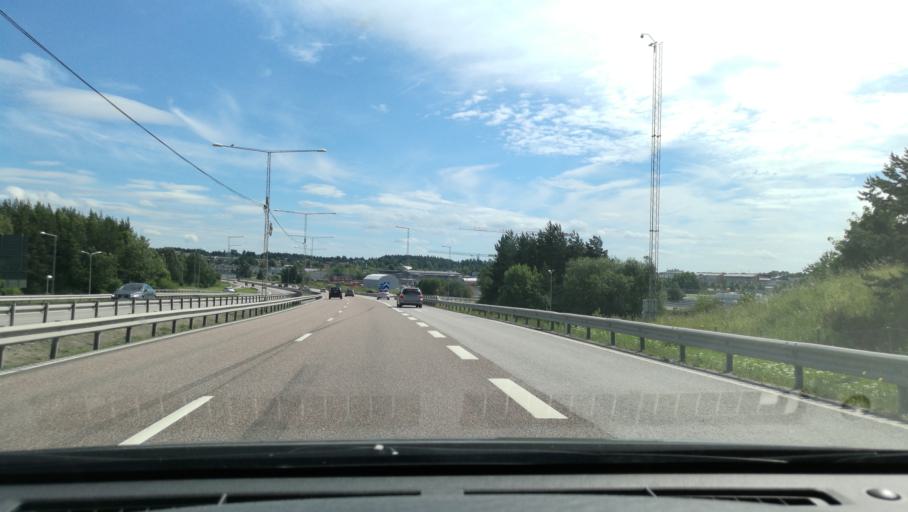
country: SE
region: Stockholm
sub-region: Jarfalla Kommun
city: Jakobsberg
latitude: 59.4125
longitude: 17.8552
